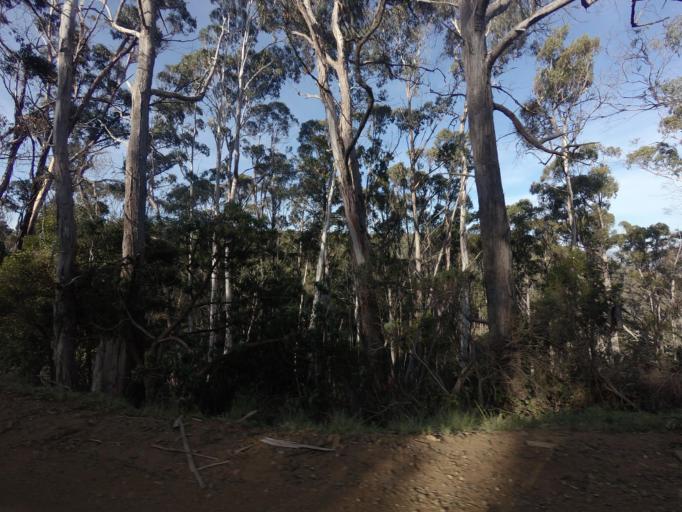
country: AU
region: Tasmania
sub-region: Brighton
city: Bridgewater
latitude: -42.4889
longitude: 147.3853
